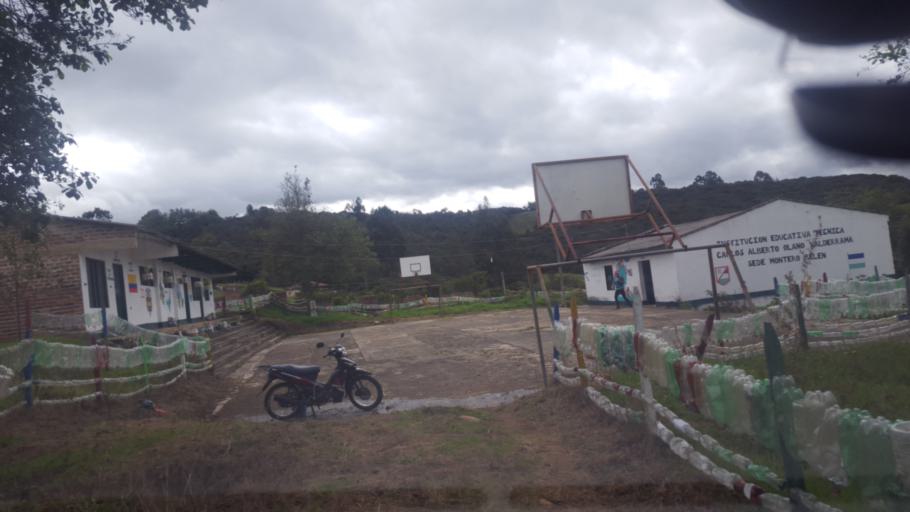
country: CO
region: Boyaca
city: Cerinza
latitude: 5.9935
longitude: -72.9509
